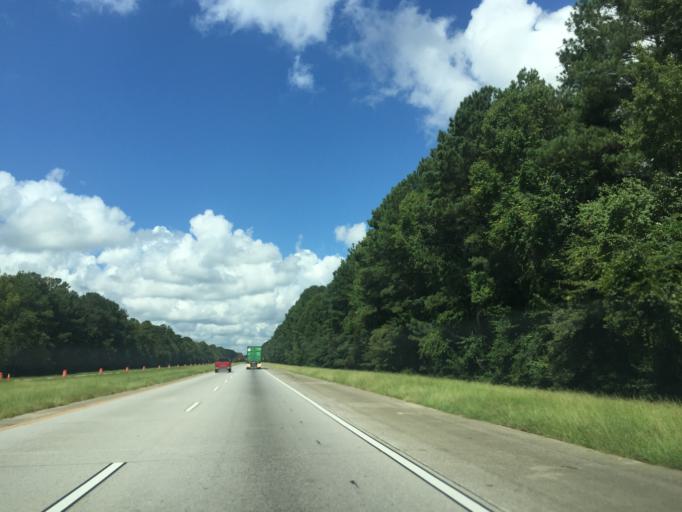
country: US
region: Georgia
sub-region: Candler County
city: Metter
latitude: 32.3757
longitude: -82.1097
